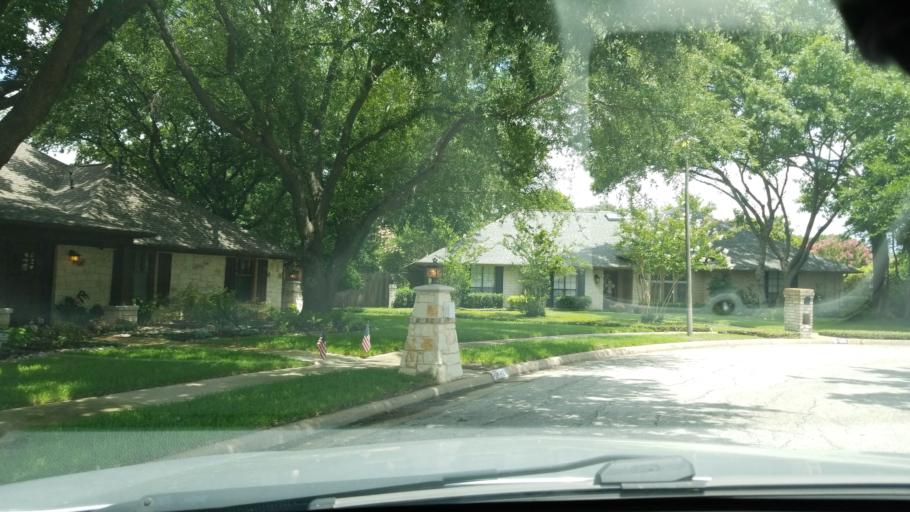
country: US
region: Texas
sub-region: Dallas County
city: Coppell
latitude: 32.9607
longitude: -96.9798
